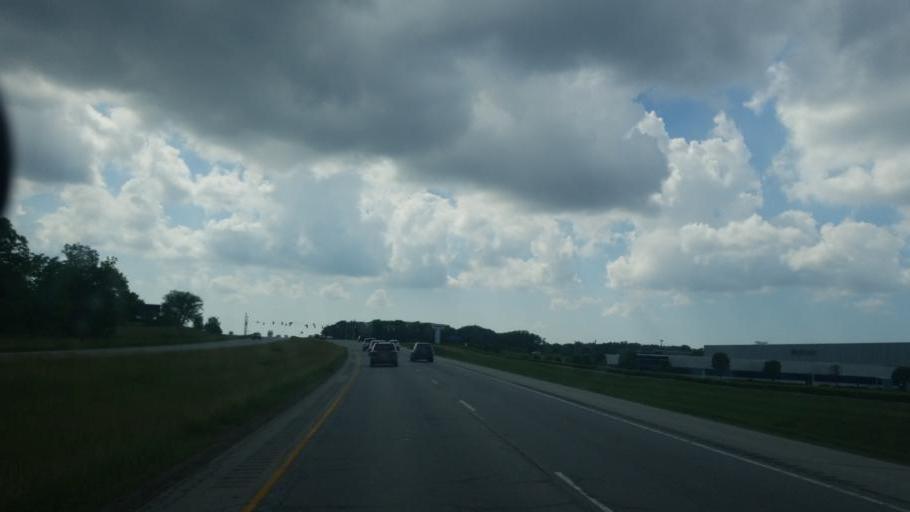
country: US
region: Indiana
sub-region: Kosciusko County
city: Warsaw
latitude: 41.2701
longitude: -85.8674
